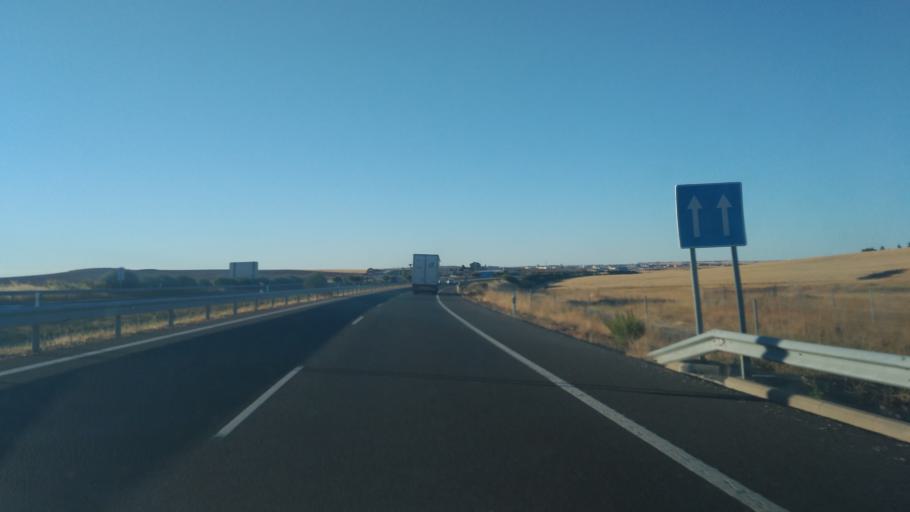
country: ES
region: Castille and Leon
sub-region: Provincia de Salamanca
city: Arapiles
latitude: 40.9006
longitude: -5.6622
